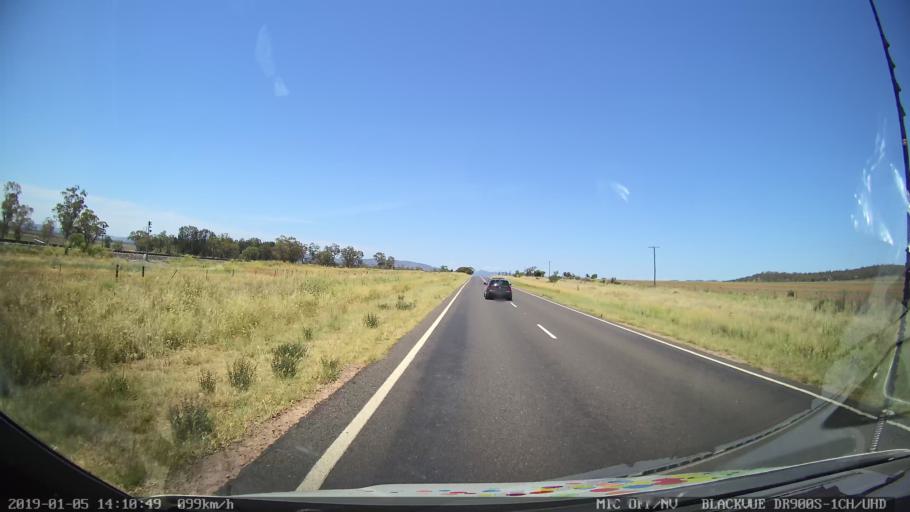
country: AU
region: New South Wales
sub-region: Gunnedah
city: Gunnedah
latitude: -31.2449
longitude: 150.4487
